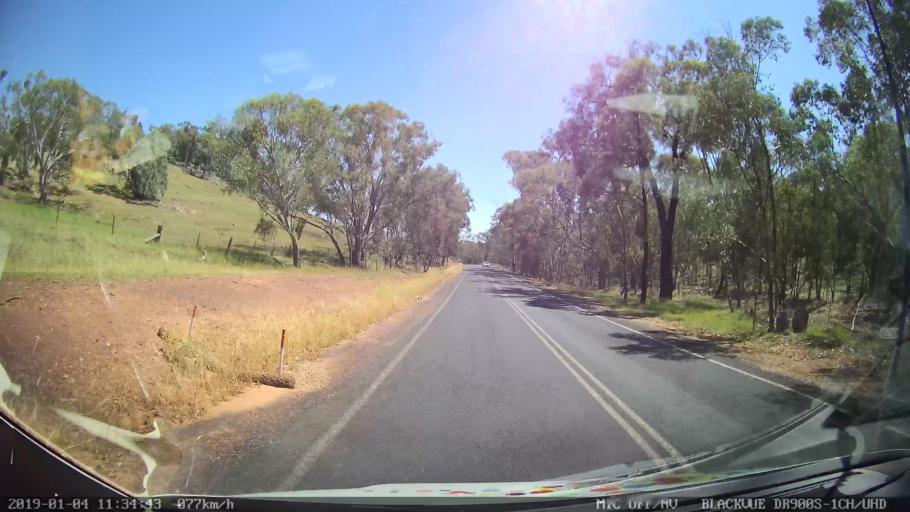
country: AU
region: New South Wales
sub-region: Cabonne
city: Molong
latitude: -33.0637
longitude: 148.8249
